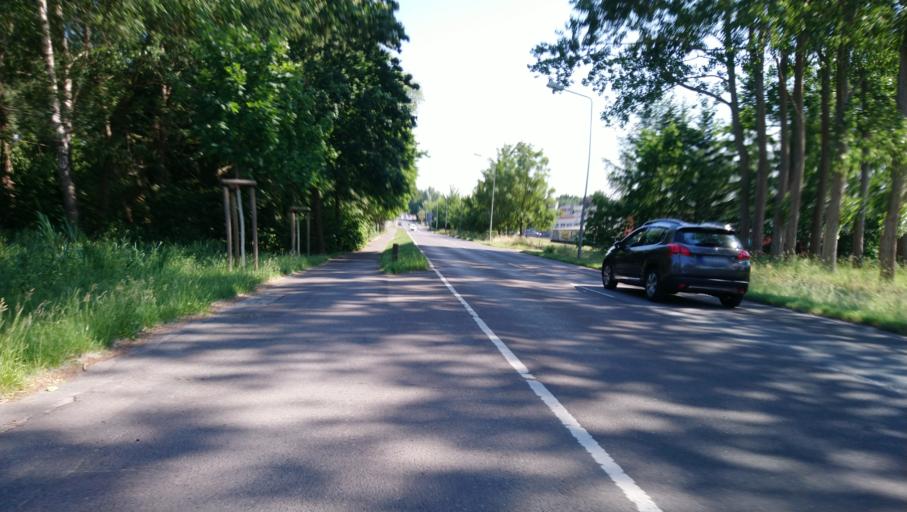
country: DE
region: Mecklenburg-Vorpommern
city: Dierkow-Neu
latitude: 54.0853
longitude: 12.1645
